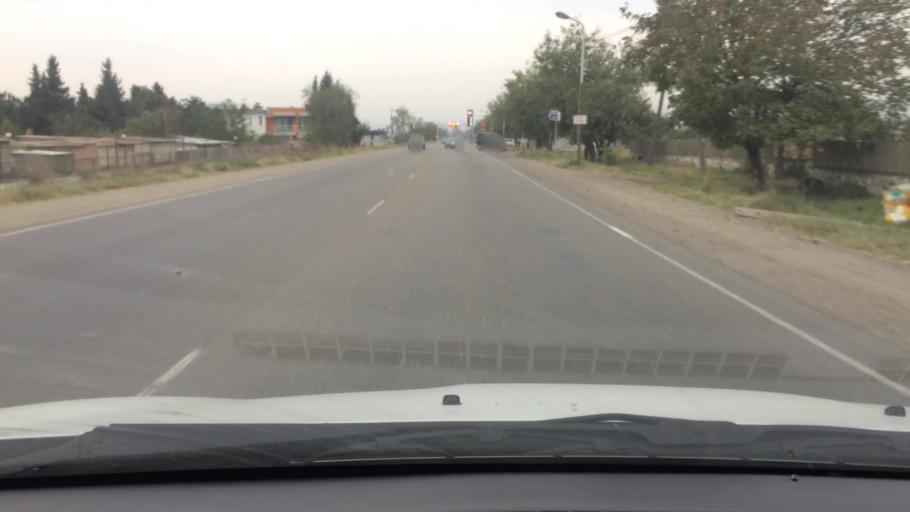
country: GE
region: Kvemo Kartli
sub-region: Marneuli
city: Marneuli
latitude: 41.5764
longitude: 44.7747
